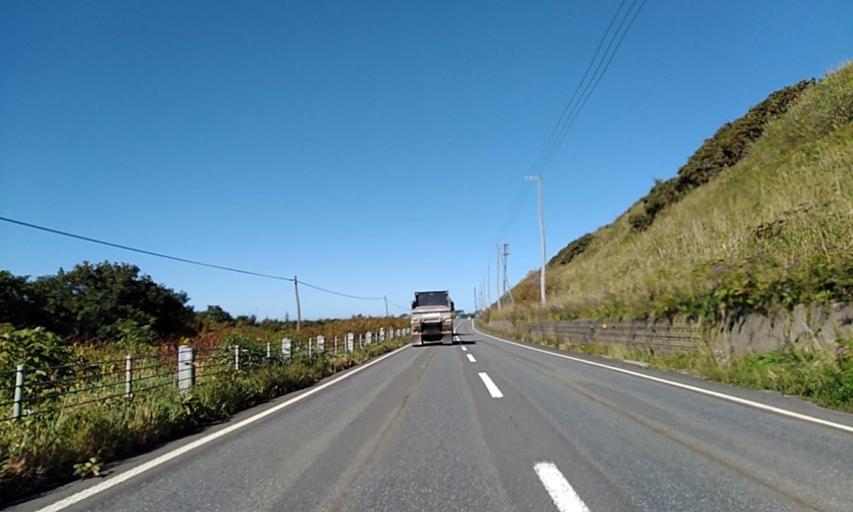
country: JP
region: Hokkaido
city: Shizunai-furukawacho
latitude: 42.4685
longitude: 142.1328
